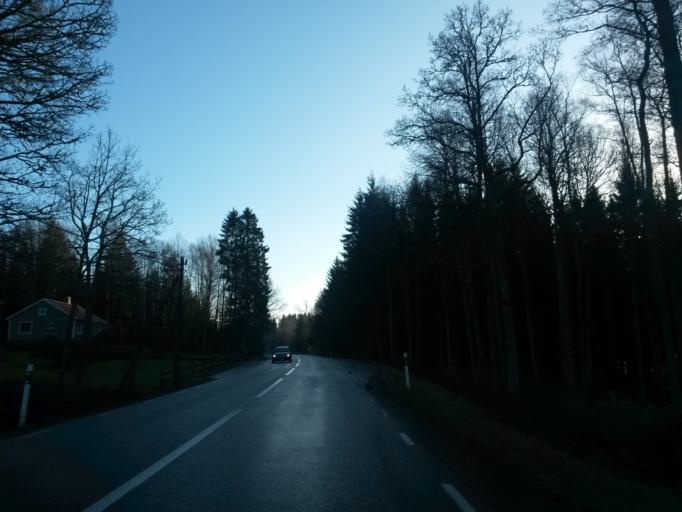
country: SE
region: Vaestra Goetaland
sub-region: Vargarda Kommun
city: Vargarda
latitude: 57.9275
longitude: 12.8591
